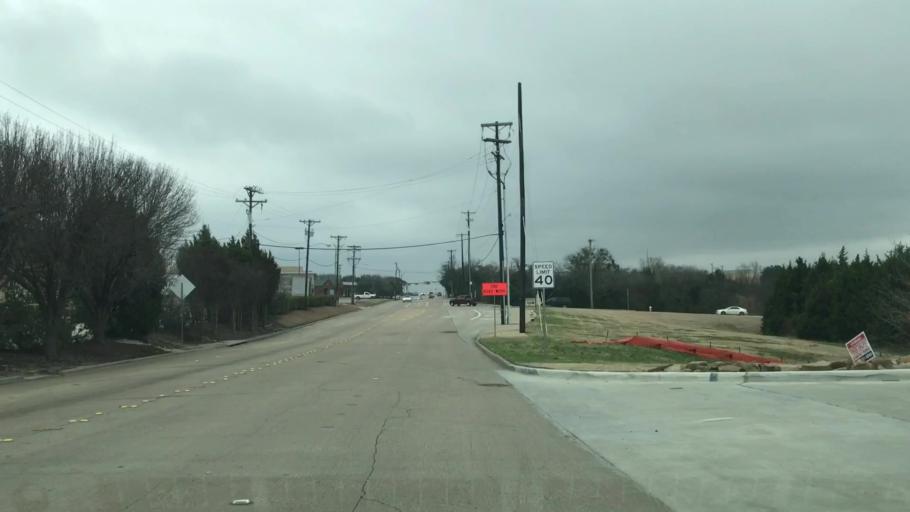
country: US
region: Texas
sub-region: Rockwall County
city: Rockwall
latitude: 32.8944
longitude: -96.4744
